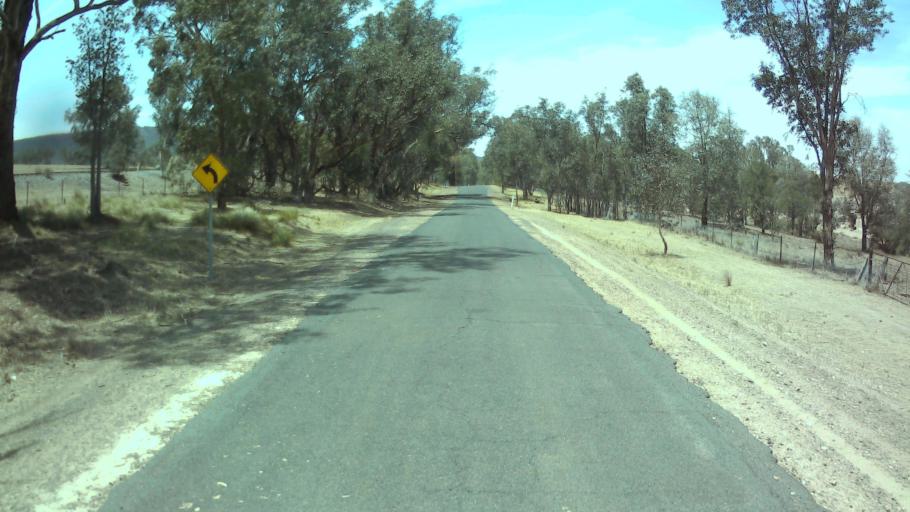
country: AU
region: New South Wales
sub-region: Weddin
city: Grenfell
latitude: -34.0256
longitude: 148.4318
